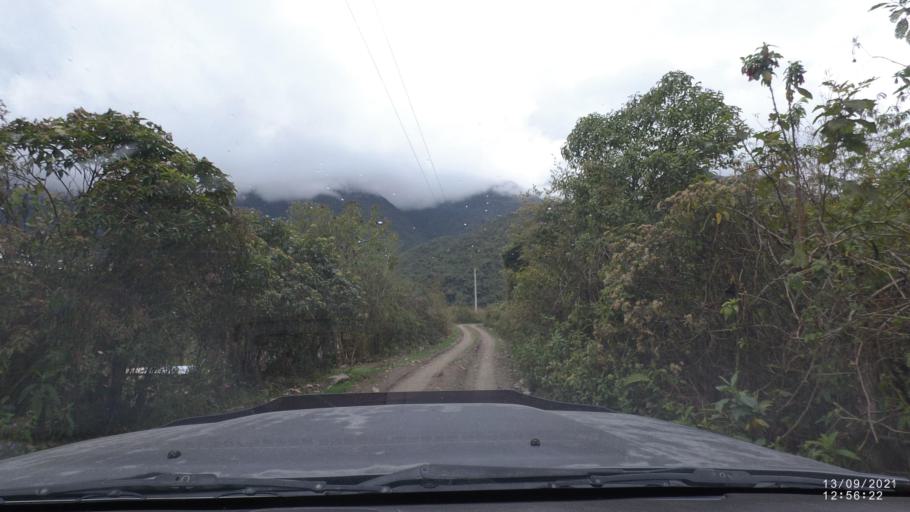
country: BO
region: Cochabamba
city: Colomi
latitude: -17.2396
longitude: -65.8202
